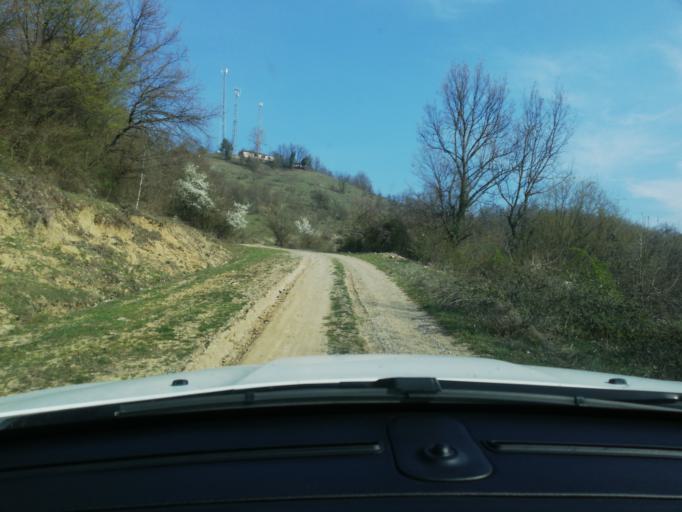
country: TR
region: Karabuk
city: Yenice
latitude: 41.2706
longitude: 32.3563
